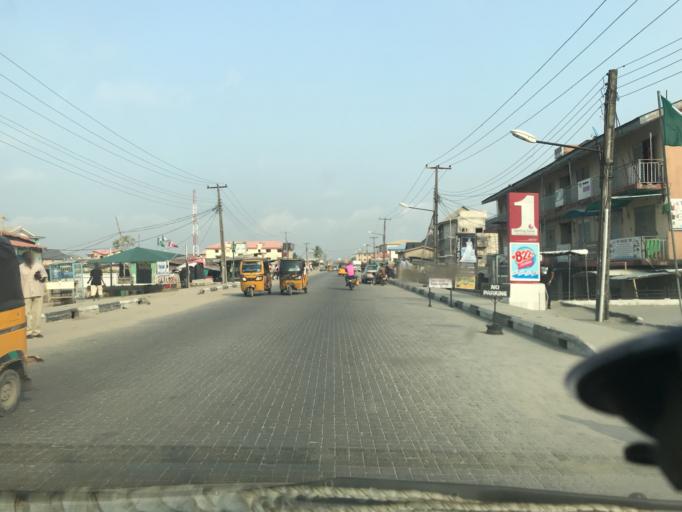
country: NG
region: Lagos
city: Ikorodu
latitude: 6.5001
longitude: 3.5842
